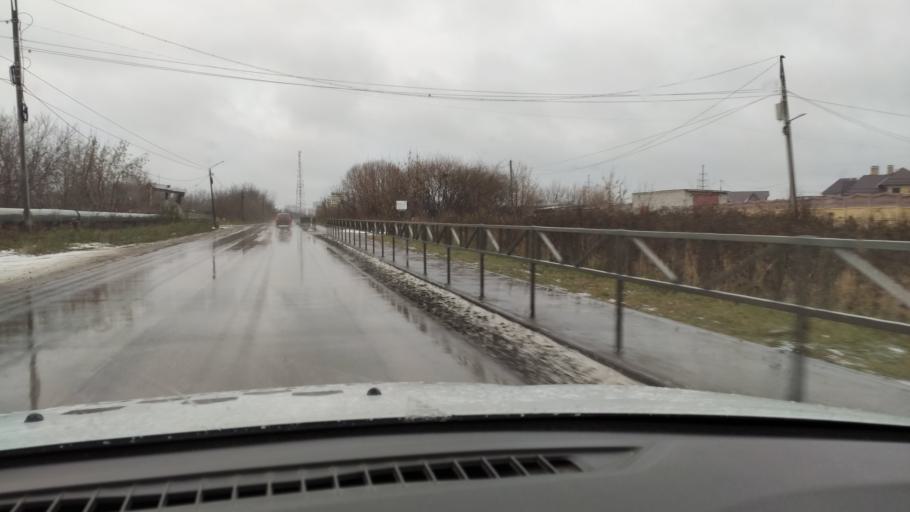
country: RU
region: Perm
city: Kondratovo
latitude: 57.9799
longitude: 56.1098
